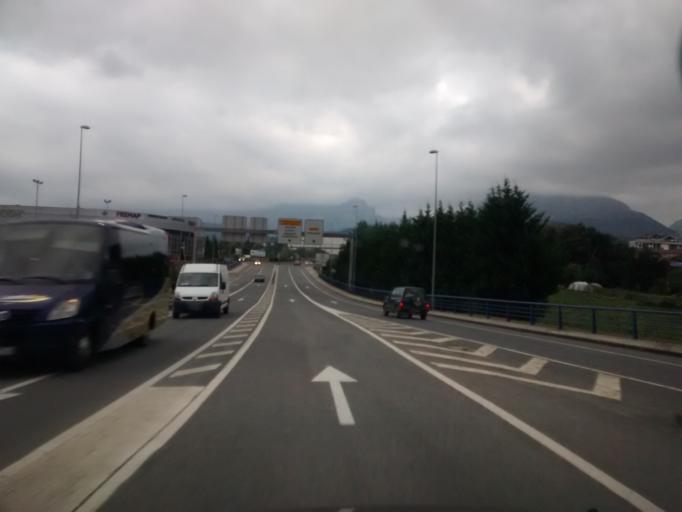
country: ES
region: Basque Country
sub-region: Bizkaia
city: Durango
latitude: 43.1716
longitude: -2.6191
